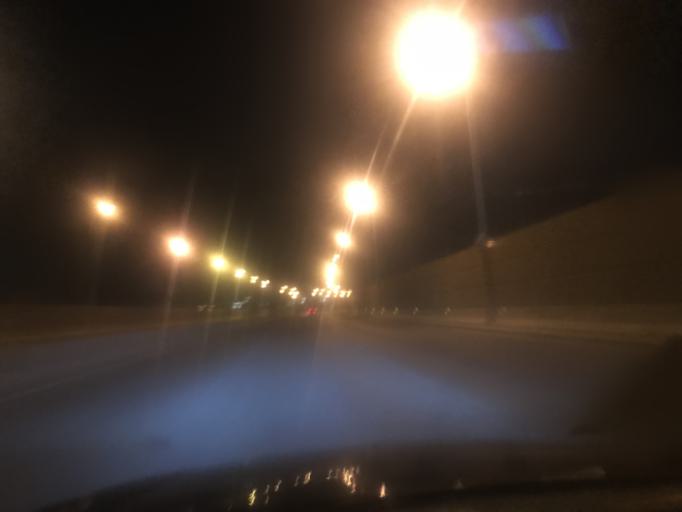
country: SA
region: Ar Riyad
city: Riyadh
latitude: 24.6941
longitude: 46.6153
